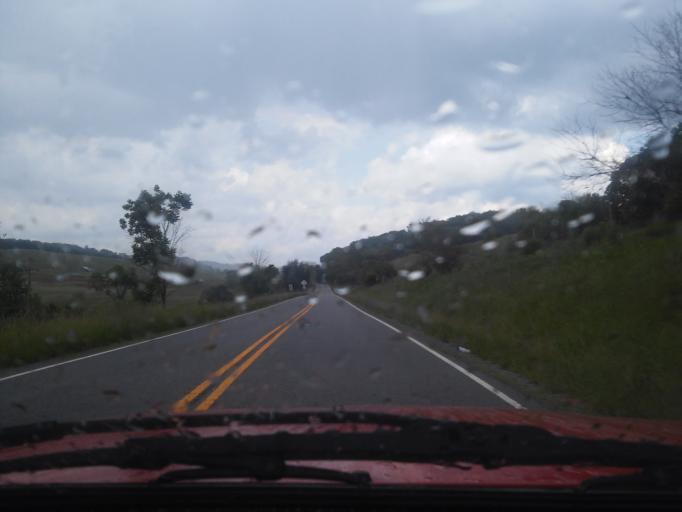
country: US
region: Virginia
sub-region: Montgomery County
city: Blacksburg
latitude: 37.3940
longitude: -80.3211
